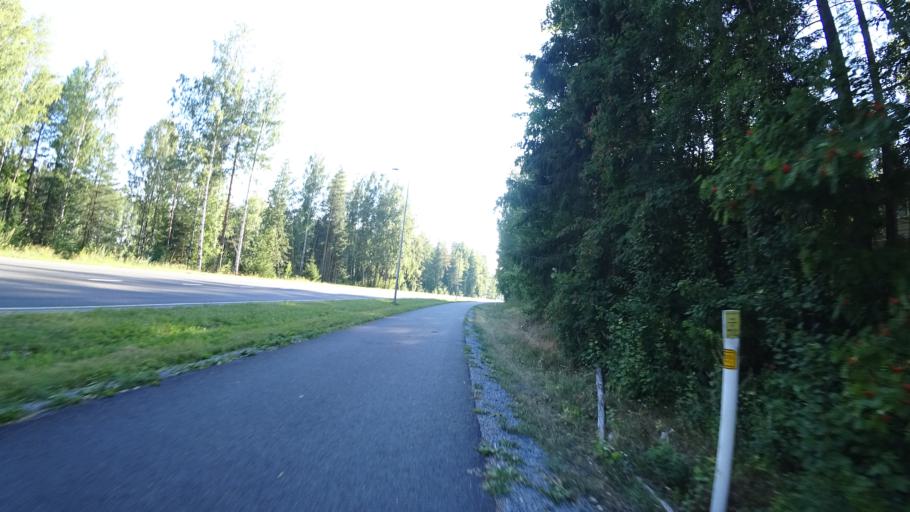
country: FI
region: Pirkanmaa
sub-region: Tampere
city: Pirkkala
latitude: 61.4939
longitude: 23.6117
